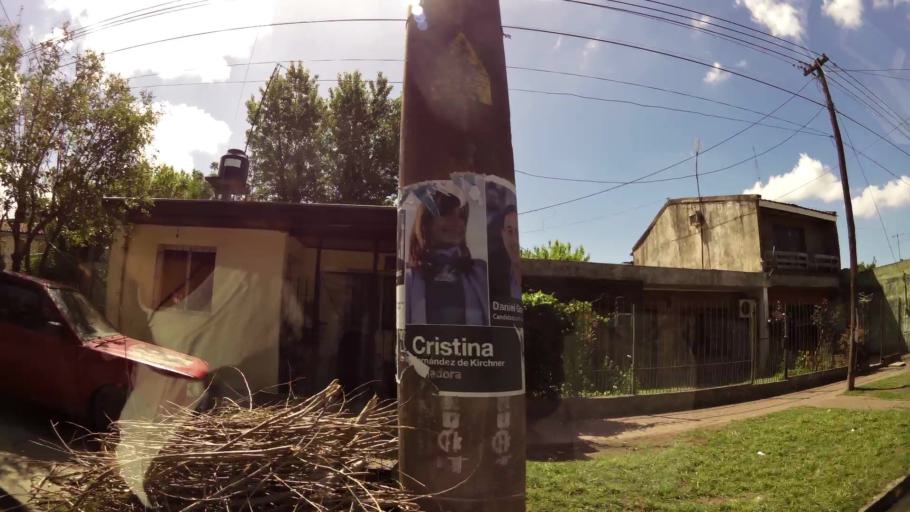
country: AR
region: Buenos Aires
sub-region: Partido de Quilmes
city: Quilmes
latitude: -34.8208
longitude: -58.2727
